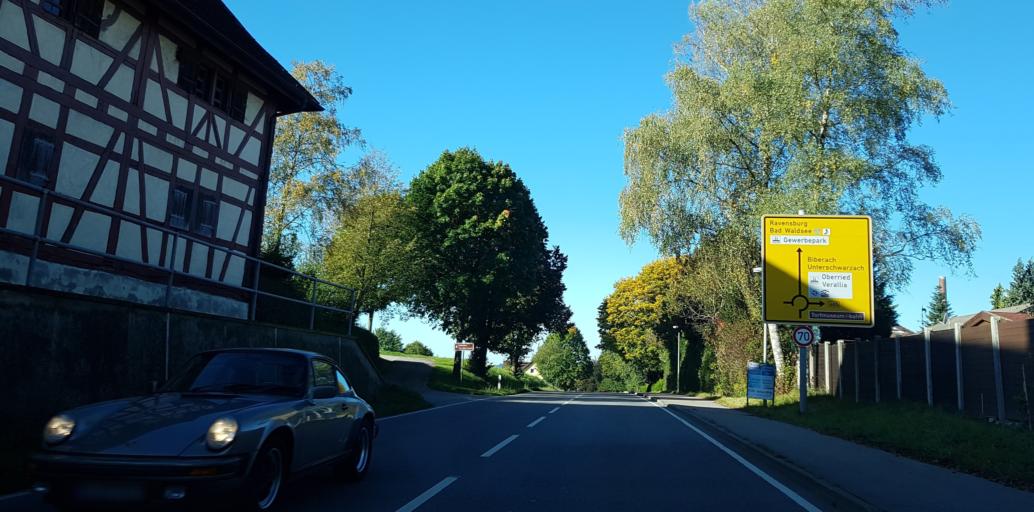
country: DE
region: Baden-Wuerttemberg
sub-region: Tuebingen Region
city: Bad Wurzach
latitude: 47.9064
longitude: 9.8840
